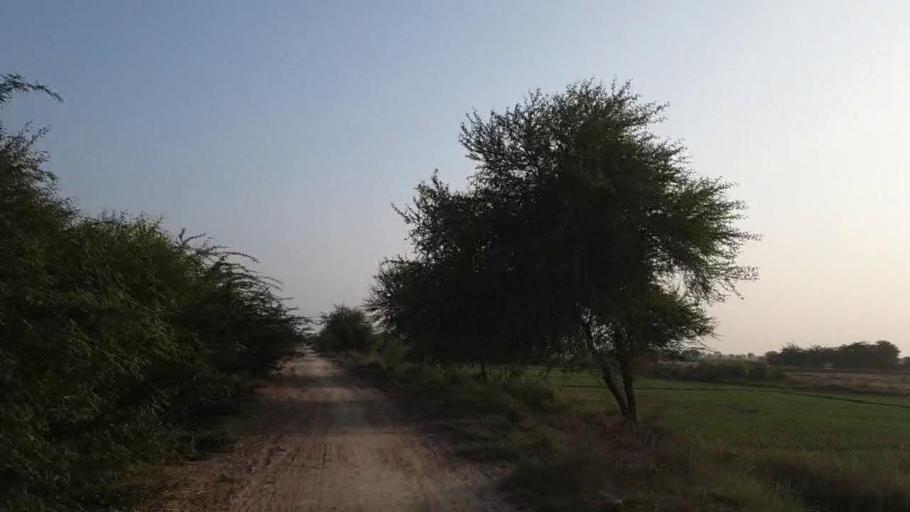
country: PK
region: Sindh
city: Kario
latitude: 24.8701
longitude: 68.6210
